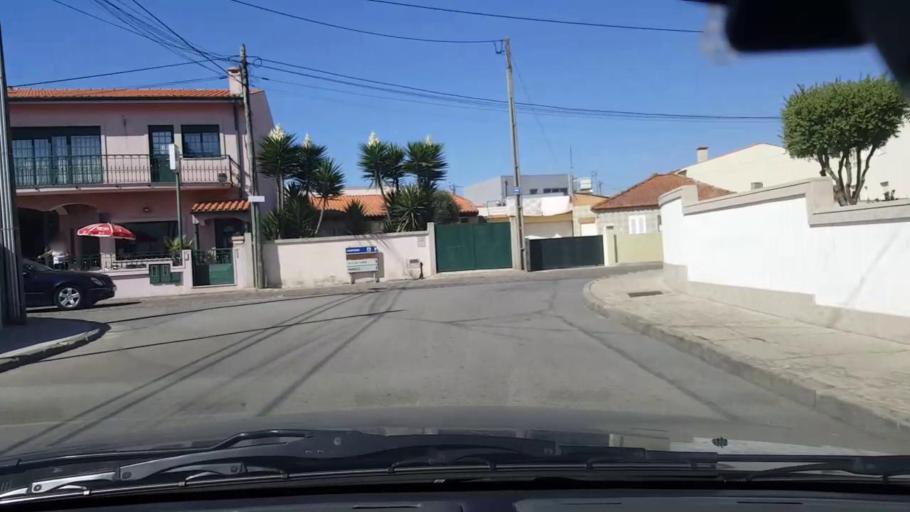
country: PT
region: Porto
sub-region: Matosinhos
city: Lavra
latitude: 41.2963
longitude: -8.7326
